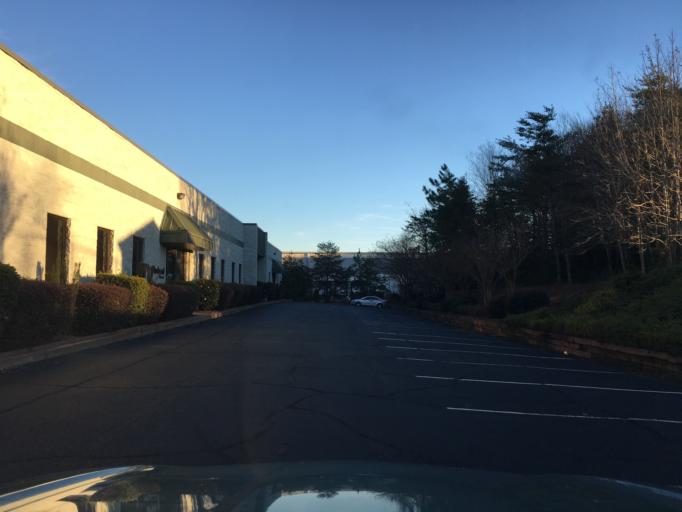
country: US
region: South Carolina
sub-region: Spartanburg County
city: Lyman
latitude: 34.9212
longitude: -82.1139
